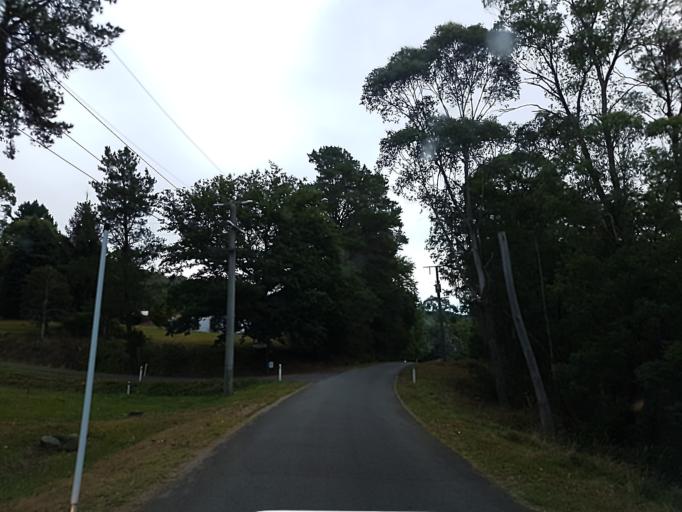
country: AU
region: Victoria
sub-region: Alpine
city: Mount Beauty
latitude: -36.8988
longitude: 147.0588
